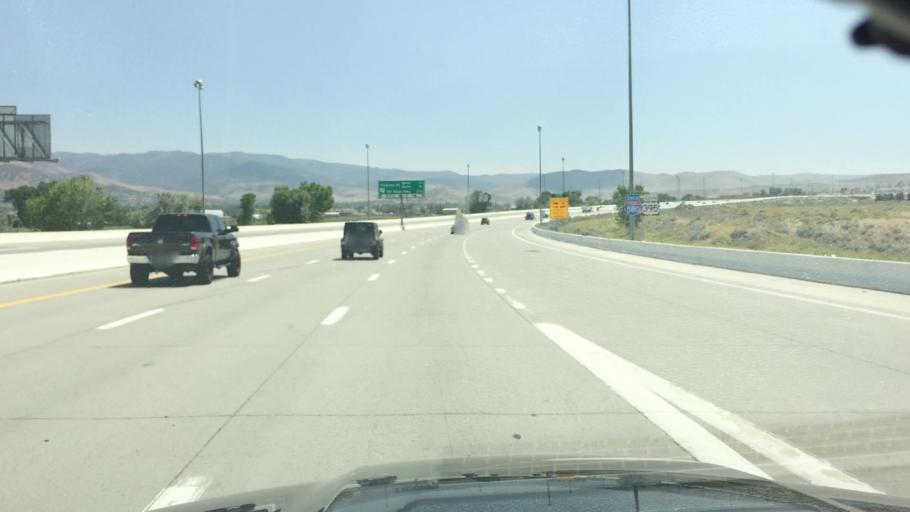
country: US
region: Nevada
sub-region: Washoe County
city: Sparks
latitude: 39.4190
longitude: -119.7478
